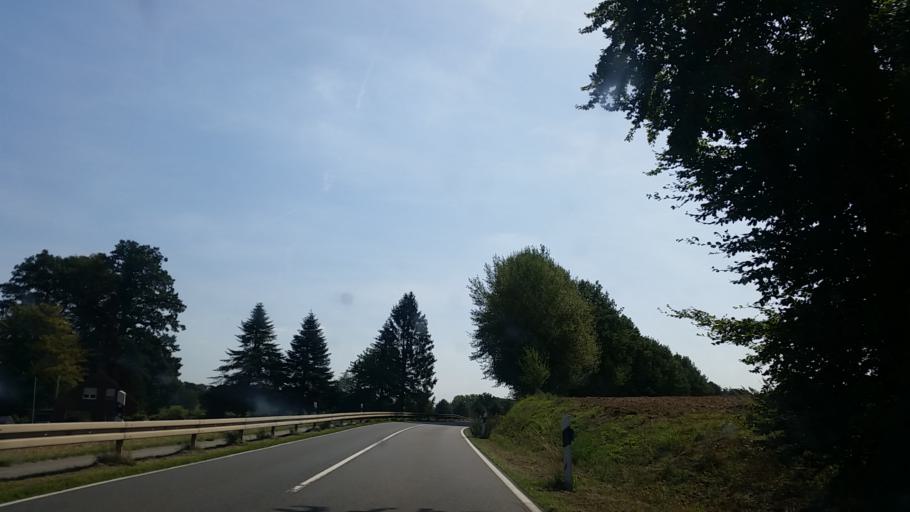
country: DE
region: Lower Saxony
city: Alfhausen
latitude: 52.5157
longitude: 7.9115
